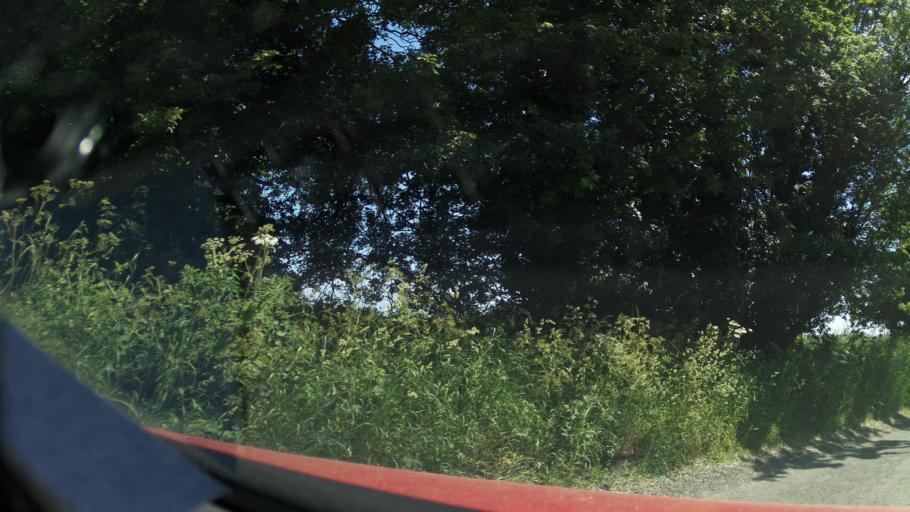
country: GB
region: England
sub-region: Wiltshire
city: Bremhill
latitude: 51.5021
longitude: -2.0496
